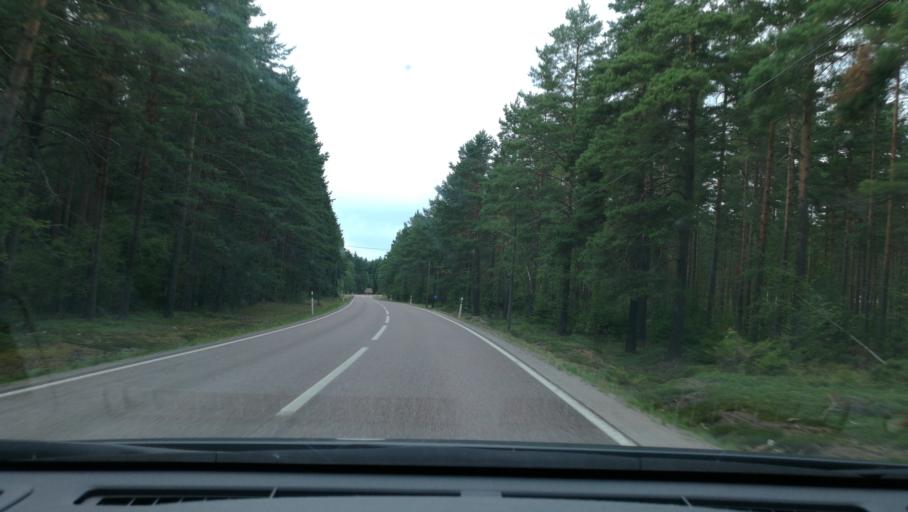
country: SE
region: Vaestmanland
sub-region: Kungsors Kommun
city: Kungsoer
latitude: 59.2956
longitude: 16.1091
